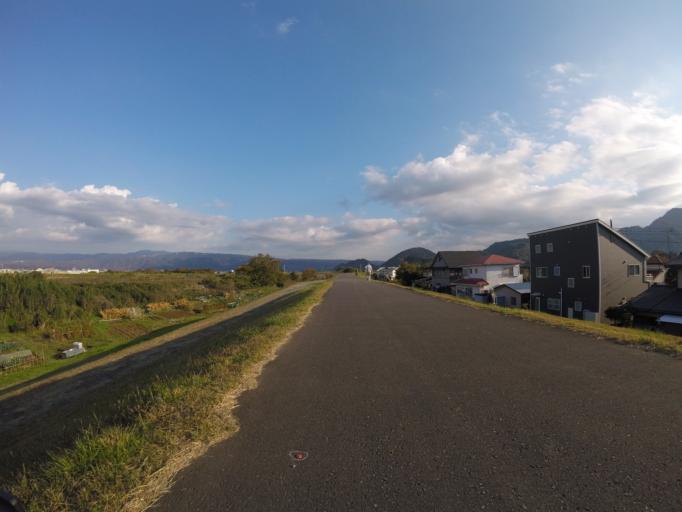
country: JP
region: Shizuoka
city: Mishima
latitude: 35.0804
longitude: 138.9095
